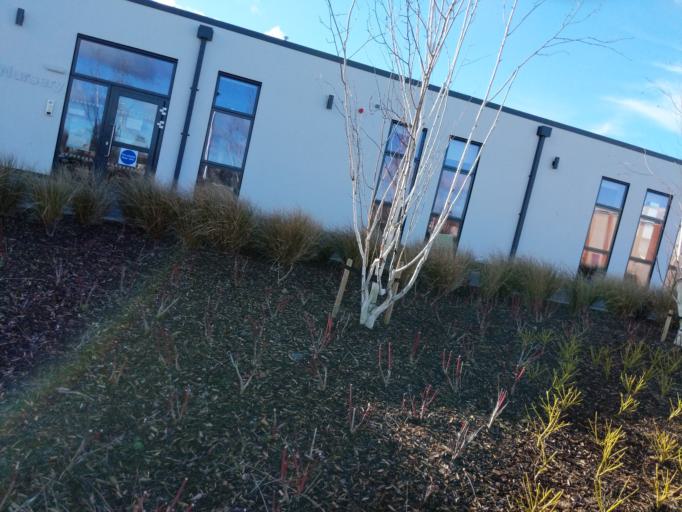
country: GB
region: Scotland
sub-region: Midlothian
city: Loanhead
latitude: 55.8563
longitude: -3.1694
